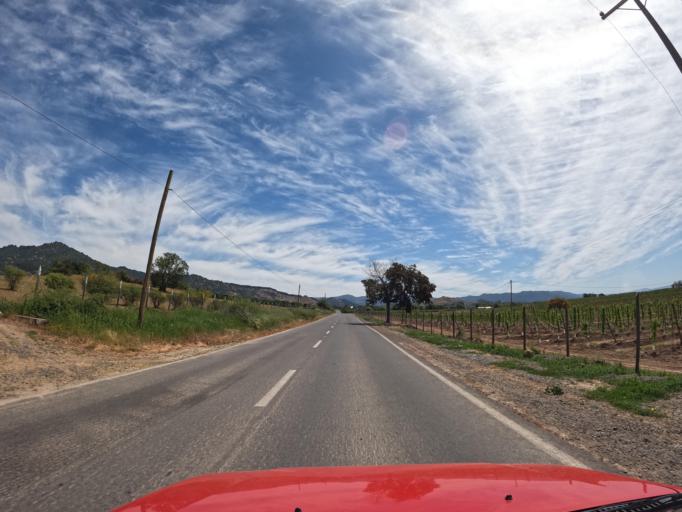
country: CL
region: Maule
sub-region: Provincia de Talca
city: Talca
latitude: -35.1218
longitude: -71.6615
